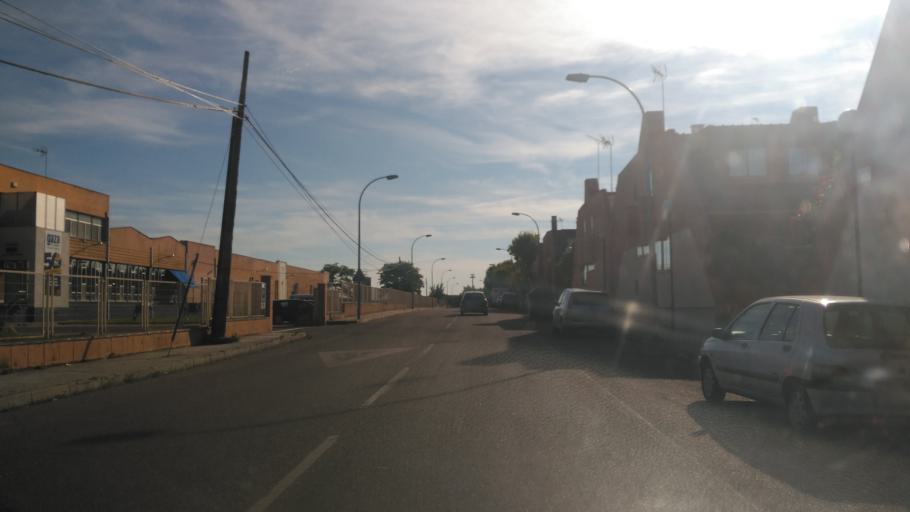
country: ES
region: Castille and Leon
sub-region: Provincia de Zamora
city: Zamora
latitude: 41.5021
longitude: -5.7577
